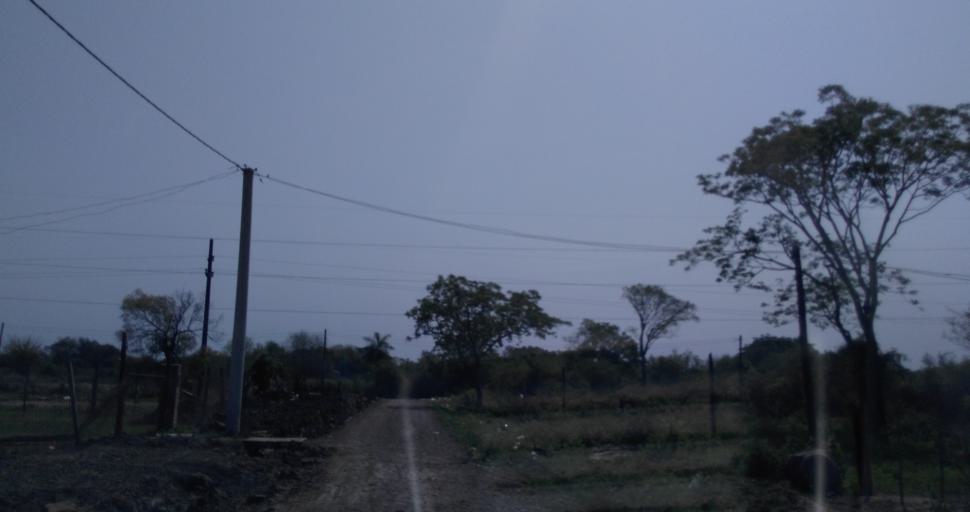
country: AR
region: Chaco
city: Fontana
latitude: -27.4158
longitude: -59.0195
